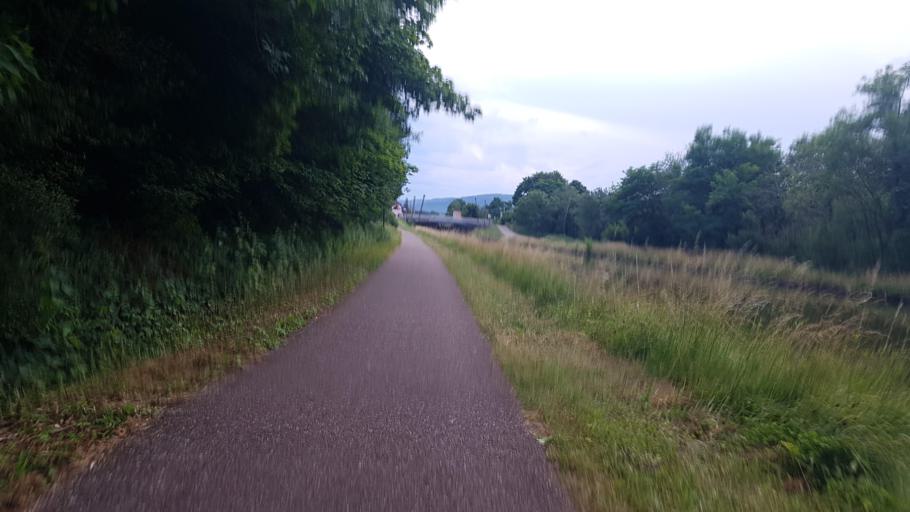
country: FR
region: Alsace
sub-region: Departement du Bas-Rhin
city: Monswiller
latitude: 48.7529
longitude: 7.3868
